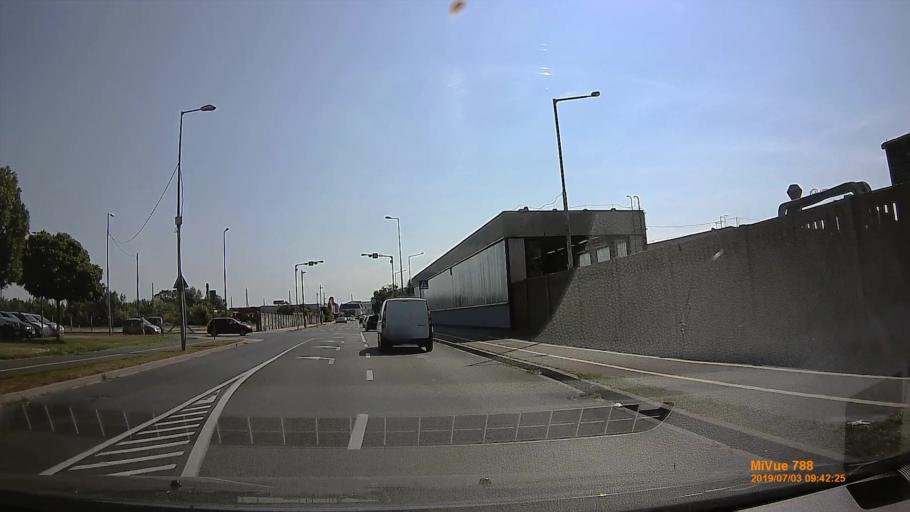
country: HU
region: Gyor-Moson-Sopron
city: Gyor
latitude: 47.6829
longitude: 17.6433
